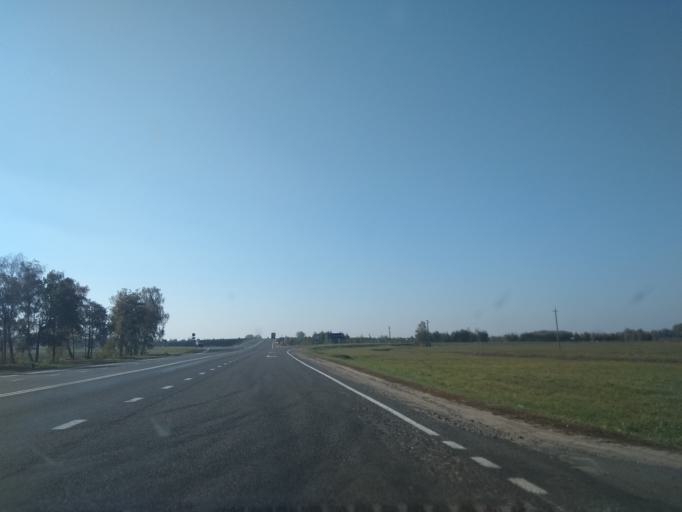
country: BY
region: Brest
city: Horad Kobryn
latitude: 52.2189
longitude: 24.4316
